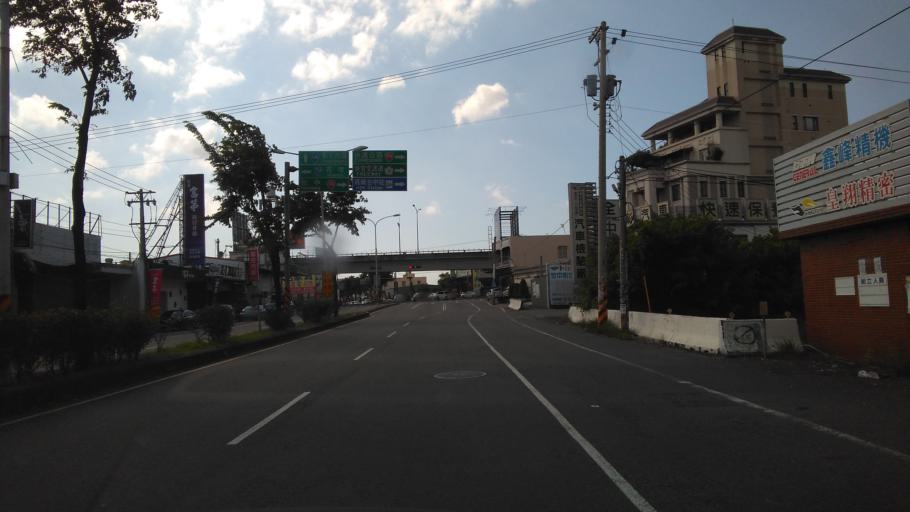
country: TW
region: Taiwan
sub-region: Changhua
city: Chang-hua
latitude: 24.0824
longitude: 120.5959
